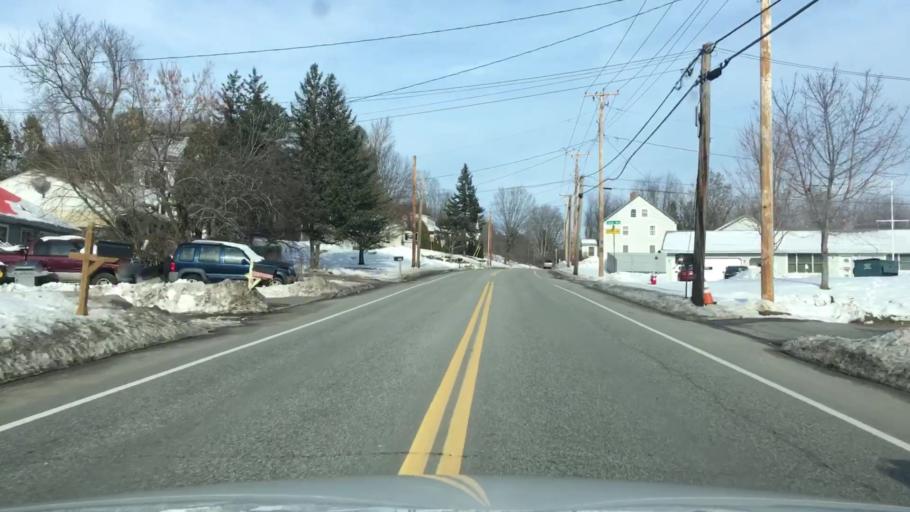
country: US
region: Maine
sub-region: Androscoggin County
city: Lewiston
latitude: 44.1318
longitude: -70.1971
